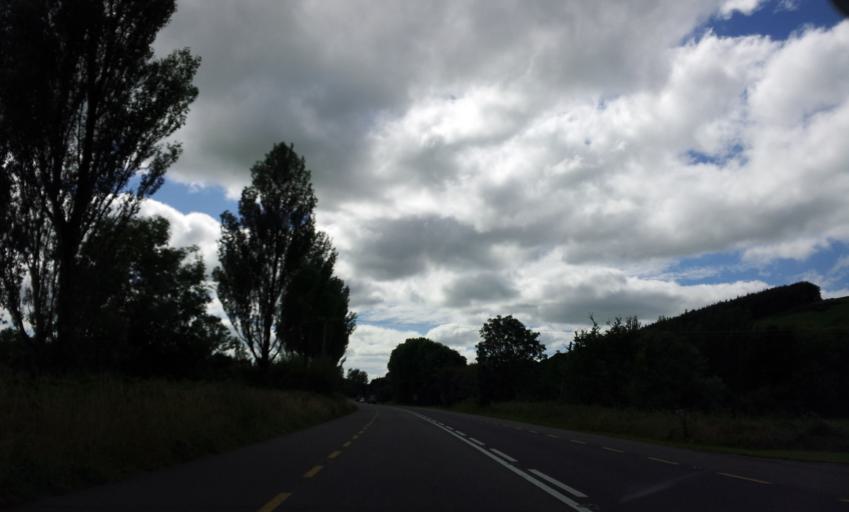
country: IE
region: Munster
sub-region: County Cork
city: Bandon
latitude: 51.8633
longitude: -8.7784
